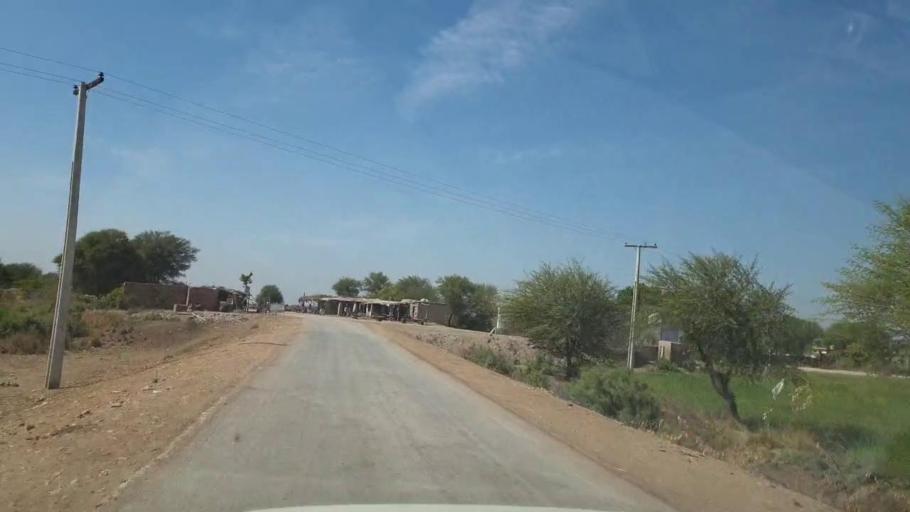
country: PK
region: Sindh
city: Mirpur Khas
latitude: 25.6472
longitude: 69.1699
